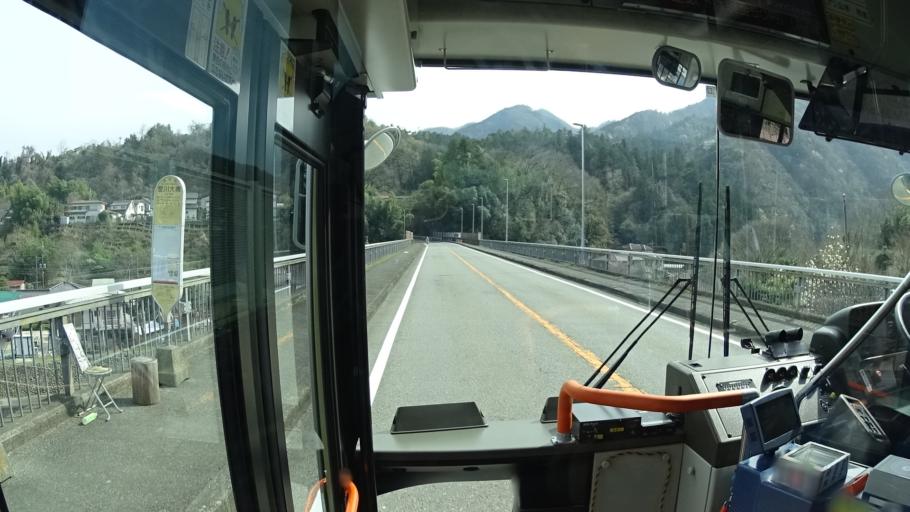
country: JP
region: Tokyo
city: Hachioji
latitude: 35.5431
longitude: 139.2619
